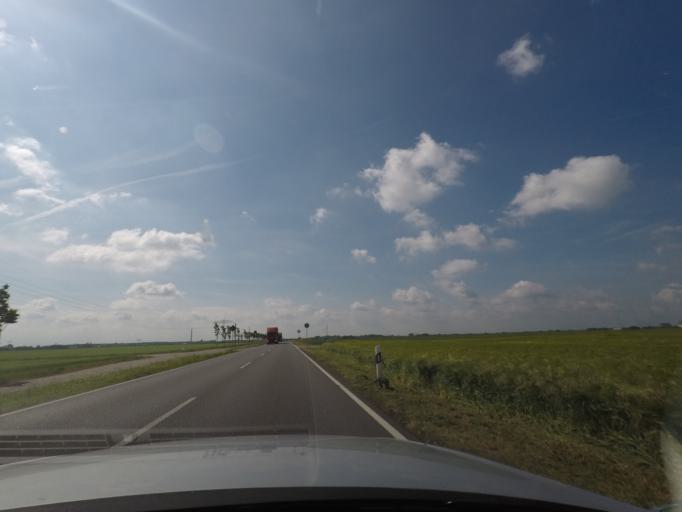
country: DE
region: Saxony
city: Markranstadt
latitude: 51.3240
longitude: 12.2081
